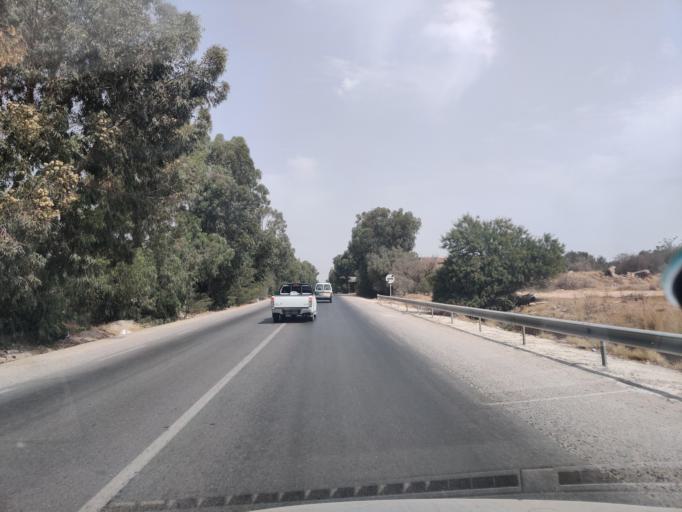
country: TN
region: Nabul
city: Al Hammamat
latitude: 36.4425
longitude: 10.5730
